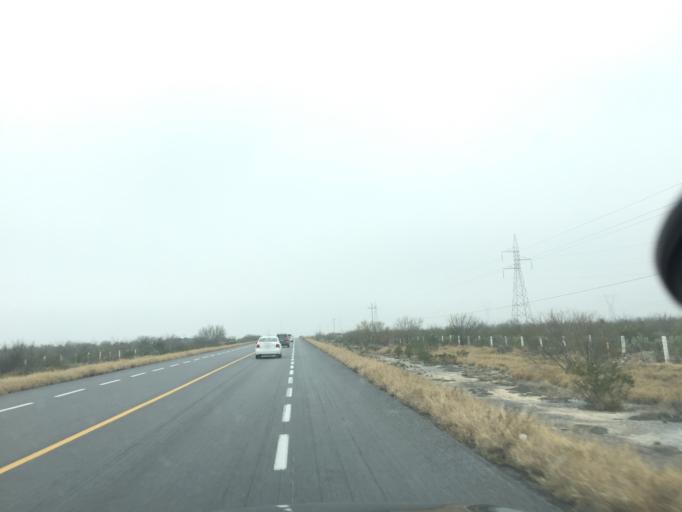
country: MX
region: Nuevo Leon
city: Bustamante
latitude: 26.4206
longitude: -100.9755
